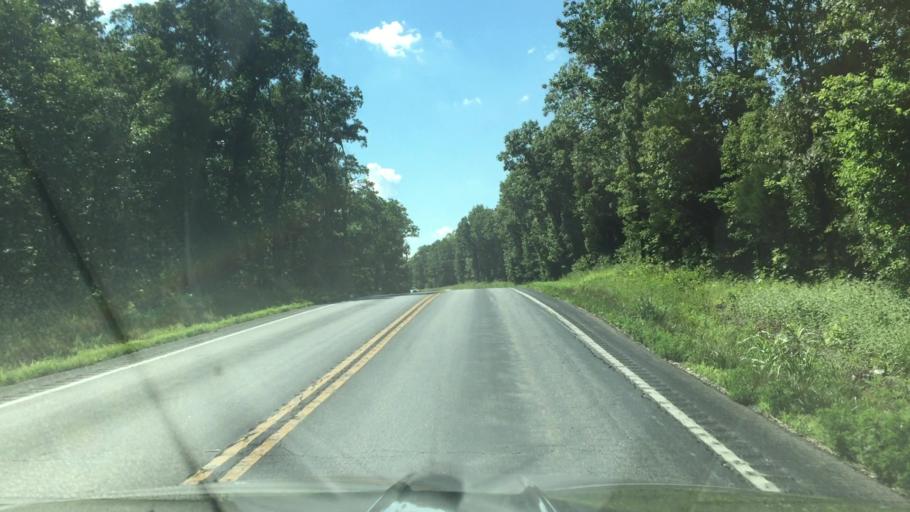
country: US
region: Missouri
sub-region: Camden County
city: Osage Beach
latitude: 38.1346
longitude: -92.5663
